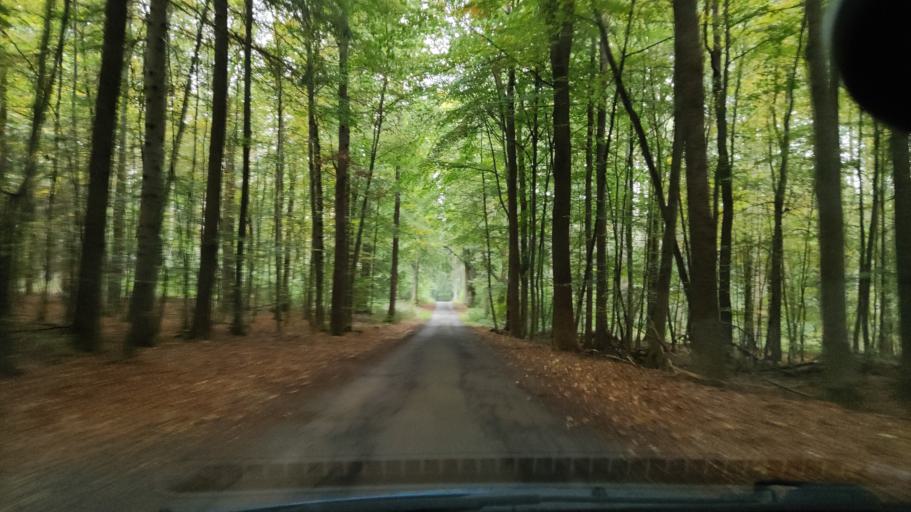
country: DE
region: Lower Saxony
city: Karwitz
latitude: 53.0889
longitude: 10.9773
